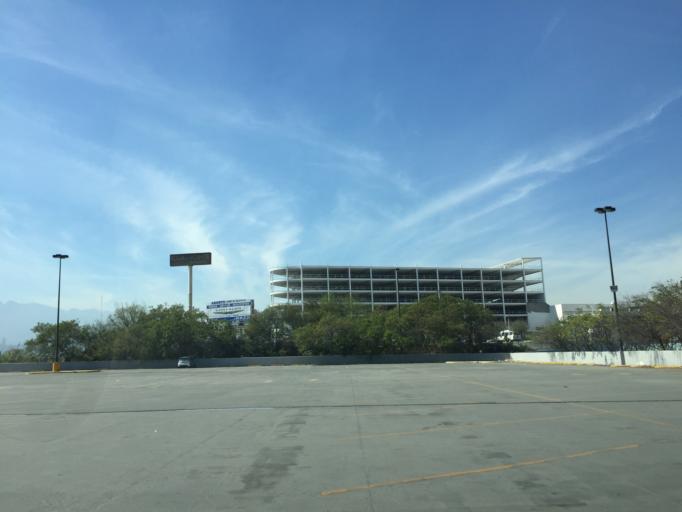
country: MX
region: Nuevo Leon
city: Guadalupe
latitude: 25.6916
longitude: -100.2414
